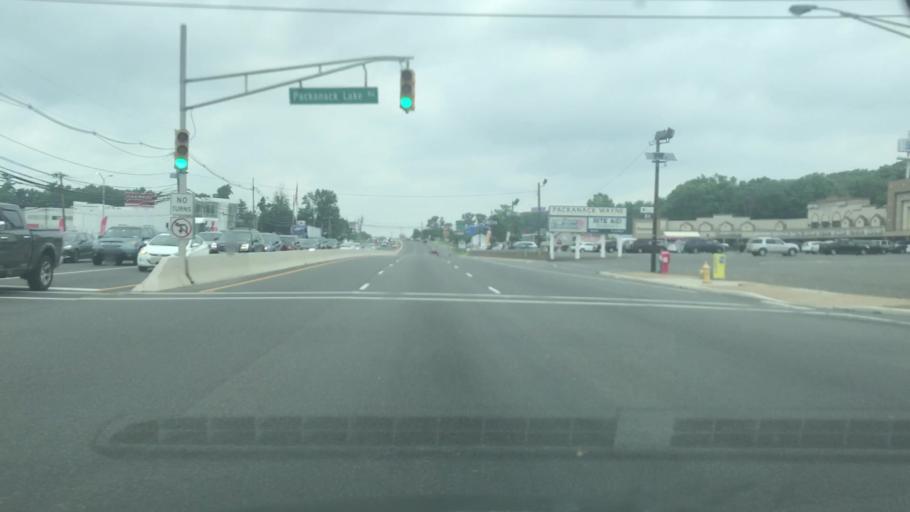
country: US
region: New Jersey
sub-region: Passaic County
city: Wayne
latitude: 40.9332
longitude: -74.2690
